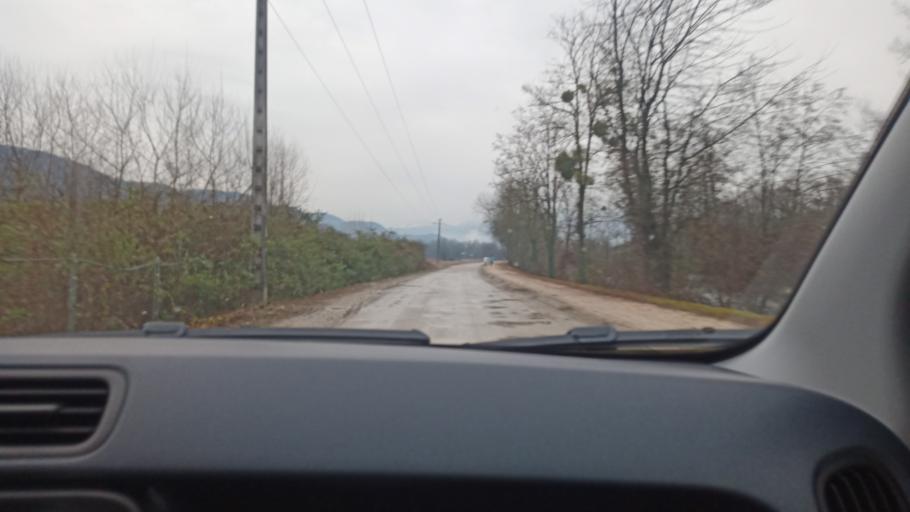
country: FR
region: Rhone-Alpes
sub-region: Departement de l'Isere
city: Domene
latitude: 45.2185
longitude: 5.8409
